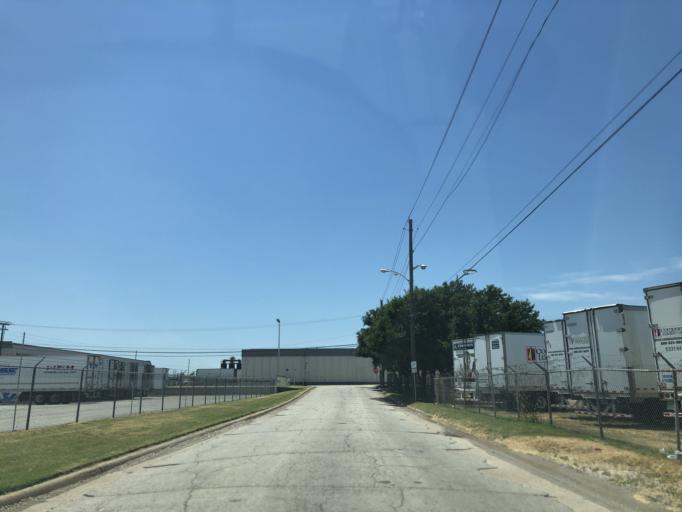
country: US
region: Texas
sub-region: Dallas County
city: Irving
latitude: 32.8126
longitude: -96.8885
